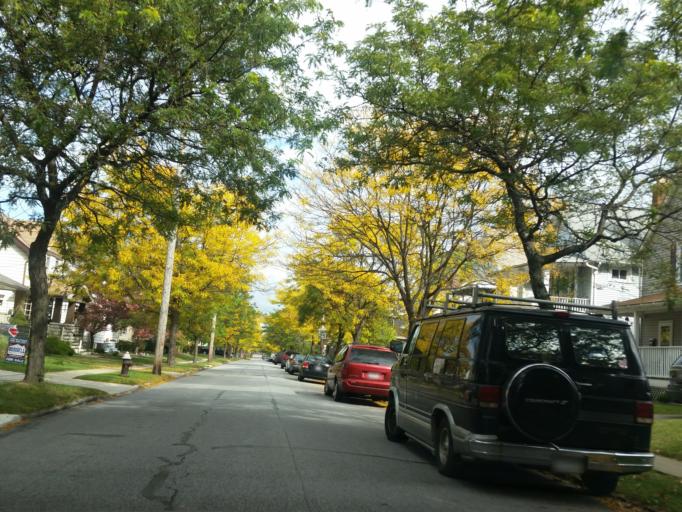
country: US
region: Ohio
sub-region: Cuyahoga County
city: Lakewood
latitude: 41.4808
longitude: -81.8167
